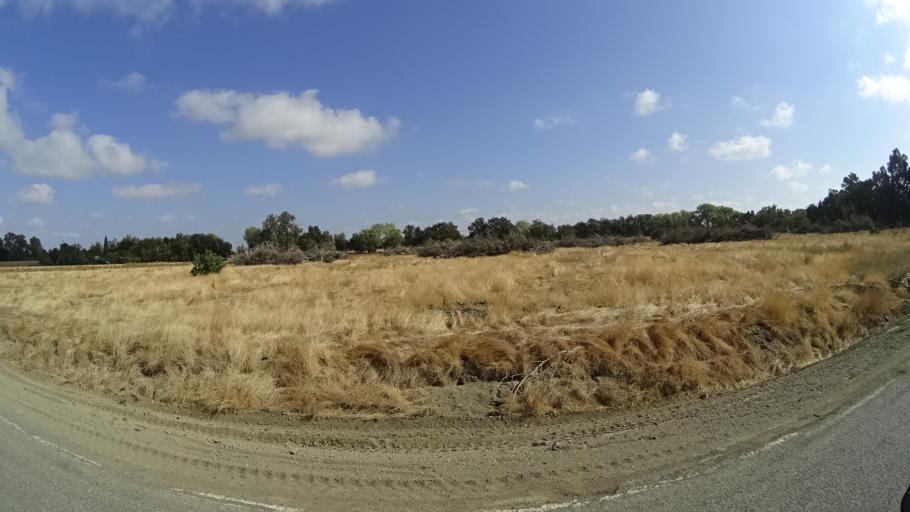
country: US
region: California
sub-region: Yolo County
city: Woodland
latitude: 38.7783
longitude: -121.6914
